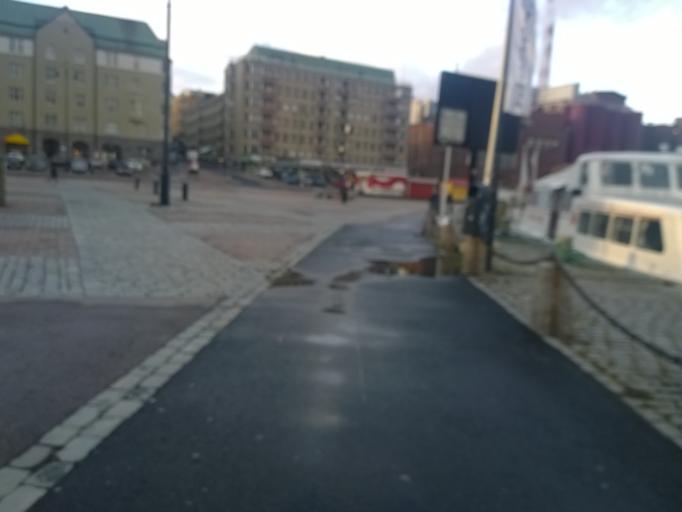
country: FI
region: Pirkanmaa
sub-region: Tampere
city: Tampere
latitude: 61.4948
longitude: 23.7606
